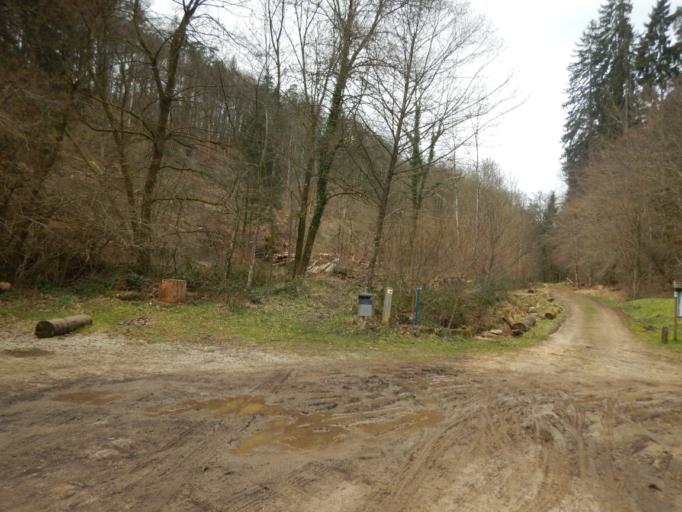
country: LU
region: Luxembourg
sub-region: Canton de Mersch
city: Tuntange
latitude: 49.7221
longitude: 6.0571
